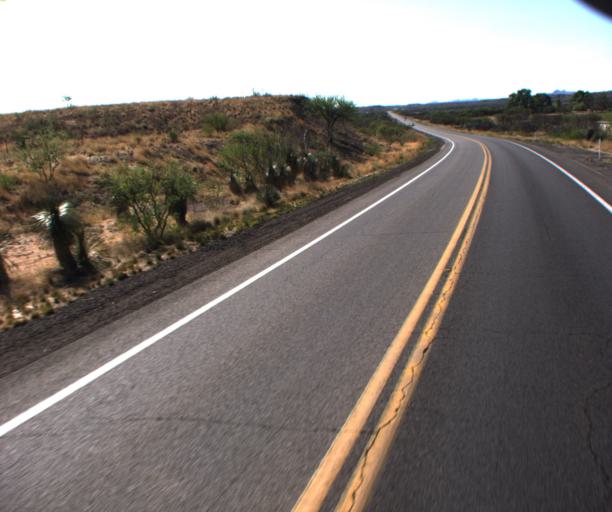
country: US
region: Arizona
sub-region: Cochise County
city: Saint David
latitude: 31.8519
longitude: -110.1998
